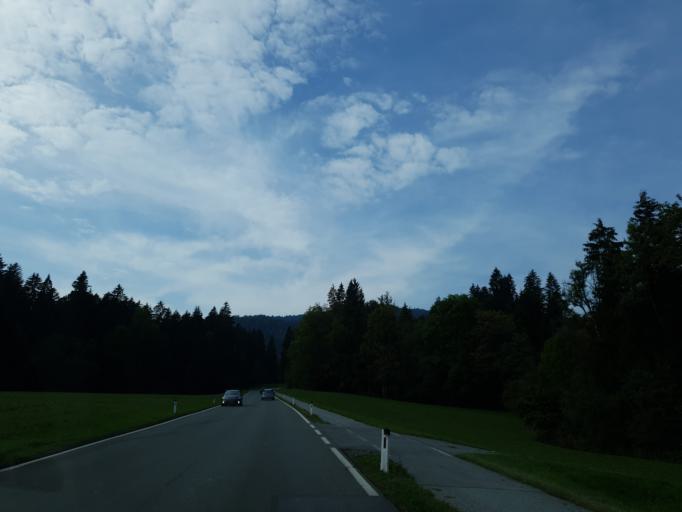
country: AT
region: Vorarlberg
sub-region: Politischer Bezirk Bregenz
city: Doren
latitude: 47.5162
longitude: 9.8558
